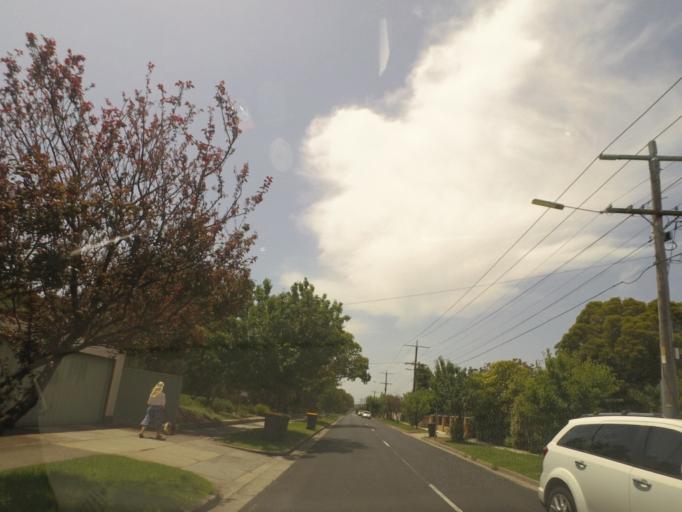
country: AU
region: Victoria
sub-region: Glen Eira
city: Bentleigh
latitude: -37.9250
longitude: 145.0294
